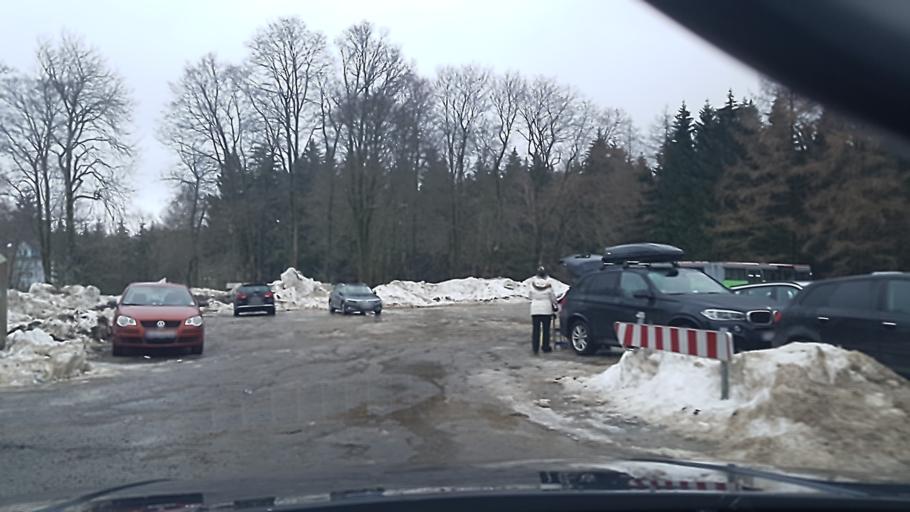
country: DE
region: Lower Saxony
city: Clausthal-Zellerfeld
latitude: 51.8599
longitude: 10.3419
